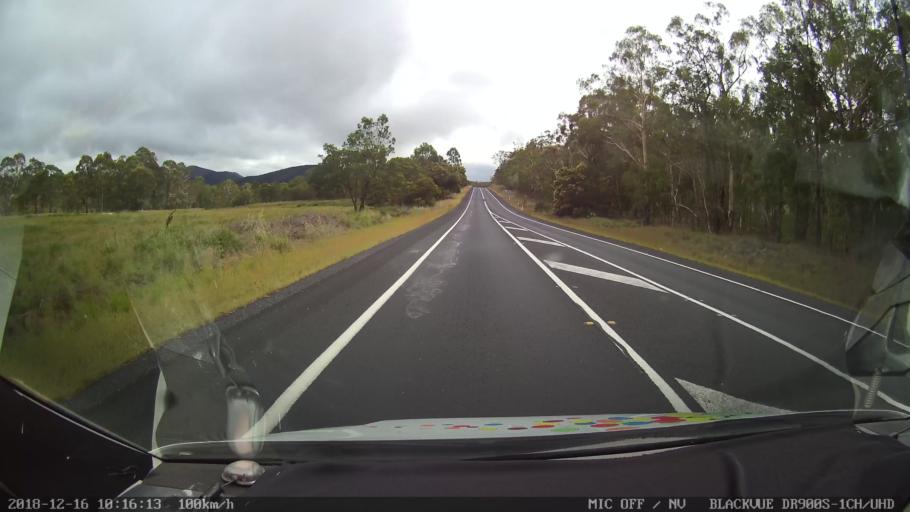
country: AU
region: New South Wales
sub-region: Tenterfield Municipality
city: Carrolls Creek
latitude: -29.2690
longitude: 151.9805
